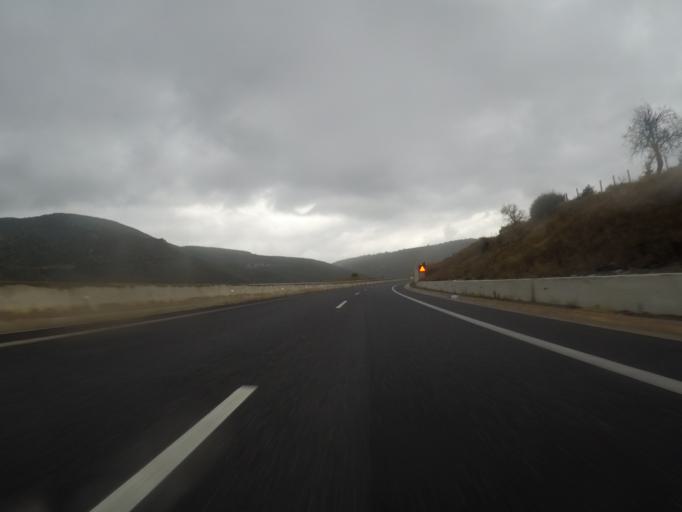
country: GR
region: Peloponnese
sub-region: Nomos Arkadias
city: Megalopoli
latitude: 37.3849
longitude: 22.2241
